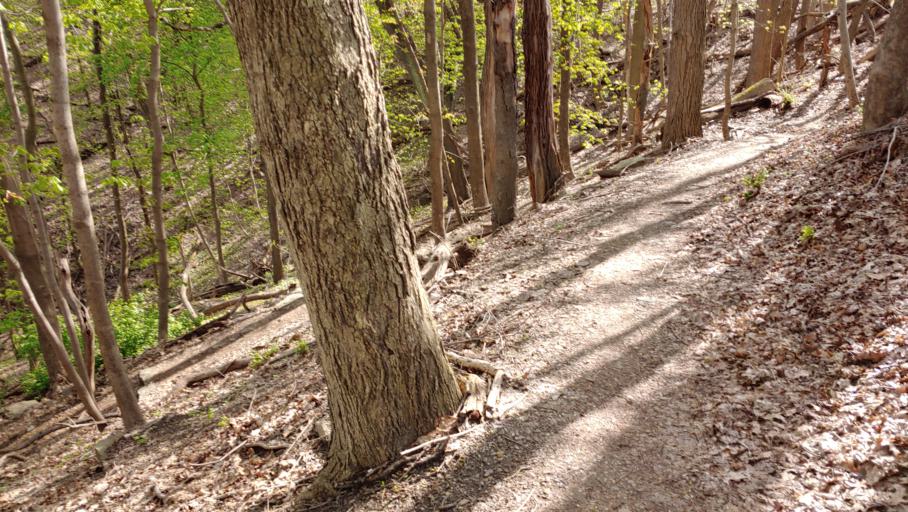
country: US
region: Pennsylvania
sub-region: Allegheny County
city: Aspinwall
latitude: 40.4815
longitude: -79.9102
